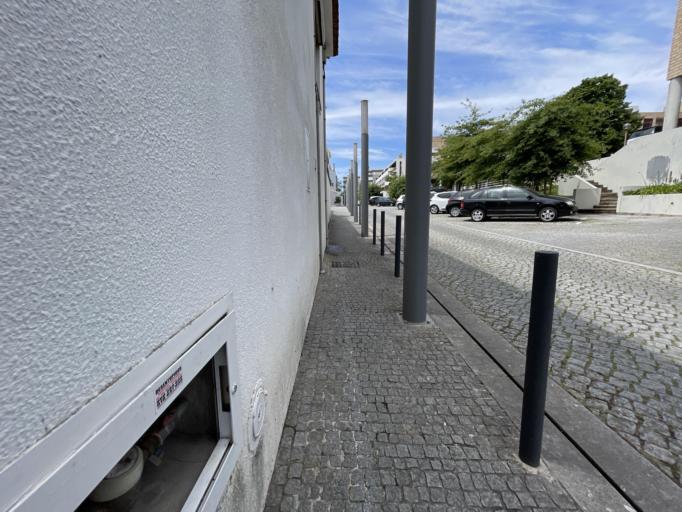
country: PT
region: Aveiro
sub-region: Ovar
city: Cortegaca
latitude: 40.9438
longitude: -8.6213
